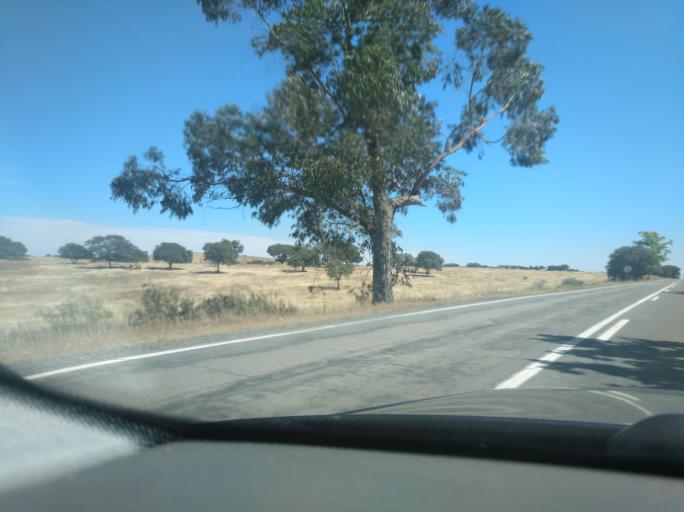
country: PT
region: Beja
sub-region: Castro Verde
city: Castro Verde
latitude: 37.6256
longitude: -8.0822
